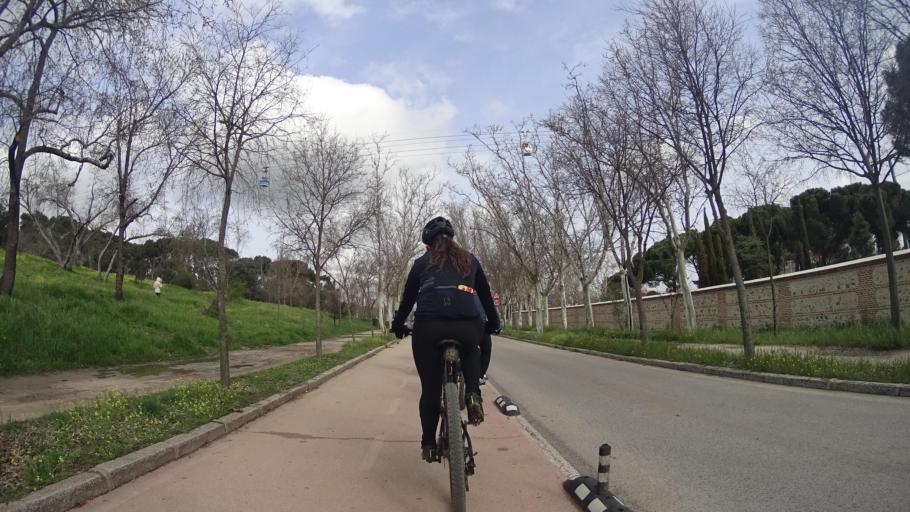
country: ES
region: Madrid
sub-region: Provincia de Madrid
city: Moncloa-Aravaca
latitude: 40.4240
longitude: -3.7325
